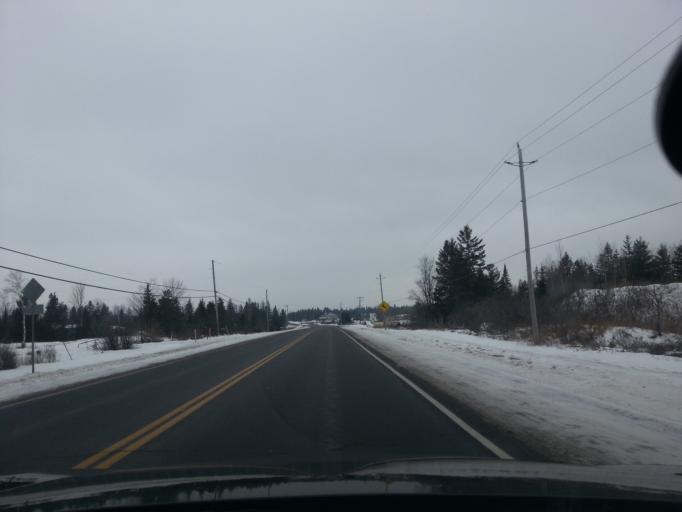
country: CA
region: Ontario
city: Carleton Place
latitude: 45.2533
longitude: -76.1551
